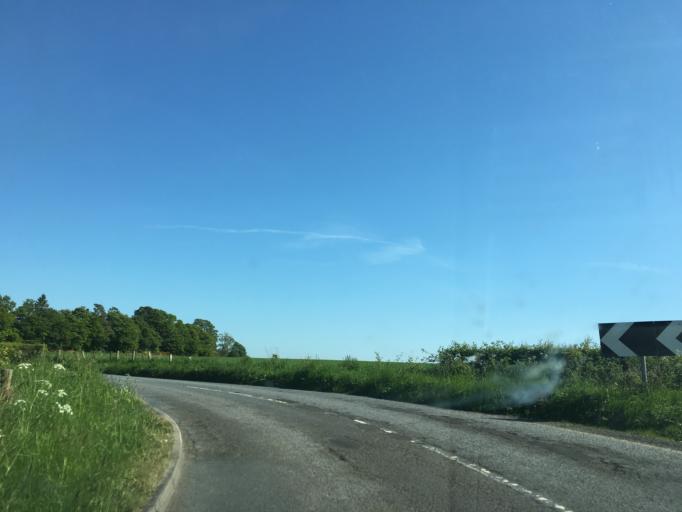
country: GB
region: Scotland
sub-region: Perth and Kinross
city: Methven
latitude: 56.3847
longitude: -3.5347
